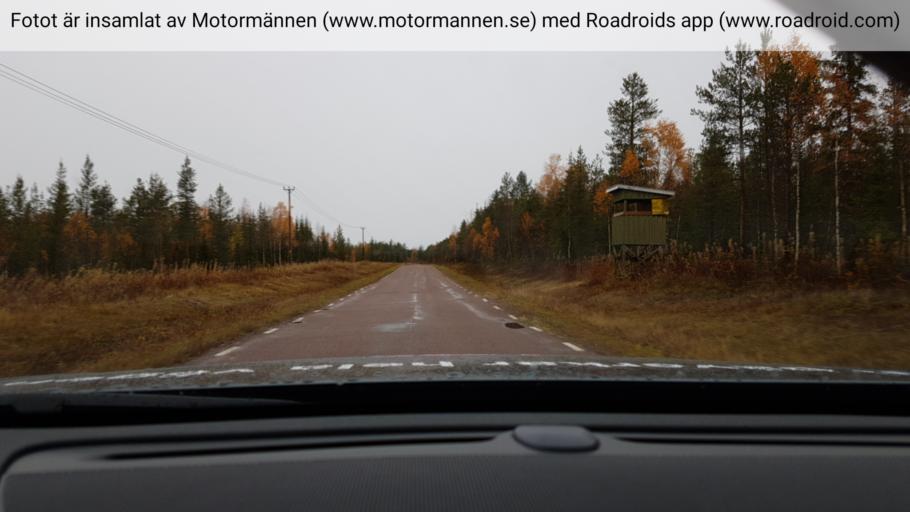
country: SE
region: Norrbotten
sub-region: Pajala Kommun
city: Pajala
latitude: 66.9518
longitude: 22.9684
